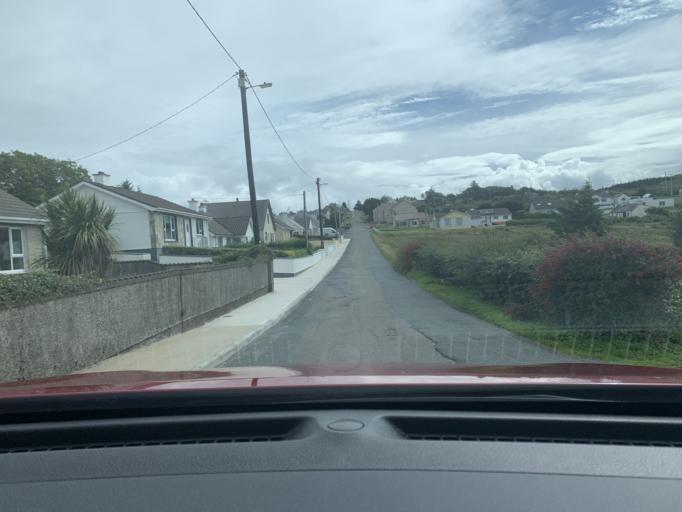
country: IE
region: Ulster
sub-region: County Donegal
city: Dungloe
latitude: 54.9469
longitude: -8.3592
